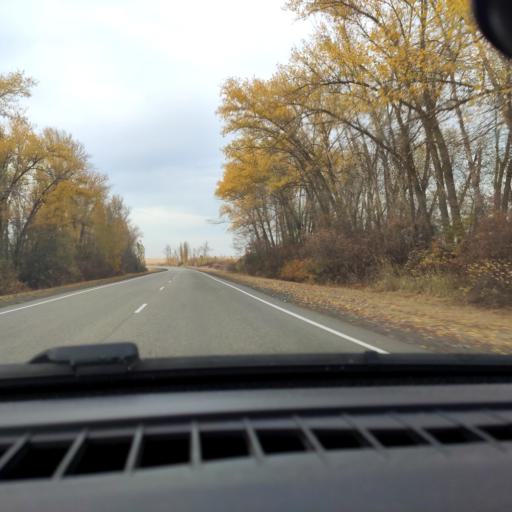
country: RU
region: Voronezj
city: Ostrogozhsk
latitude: 50.9999
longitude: 39.0009
